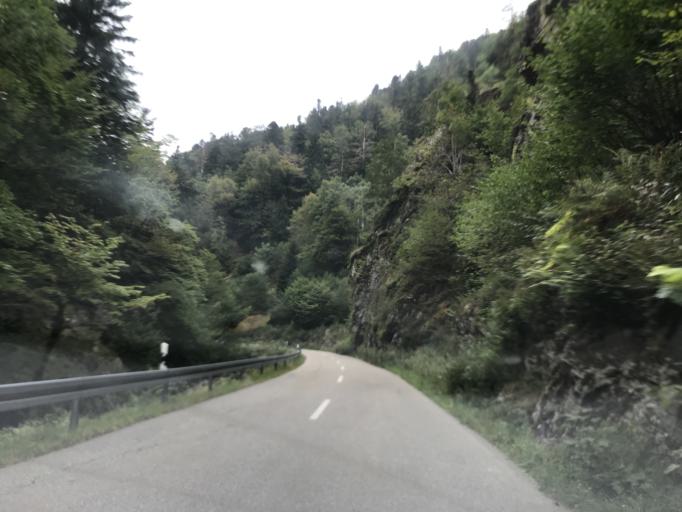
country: DE
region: Baden-Wuerttemberg
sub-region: Freiburg Region
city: Hasel
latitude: 47.6691
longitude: 7.9361
